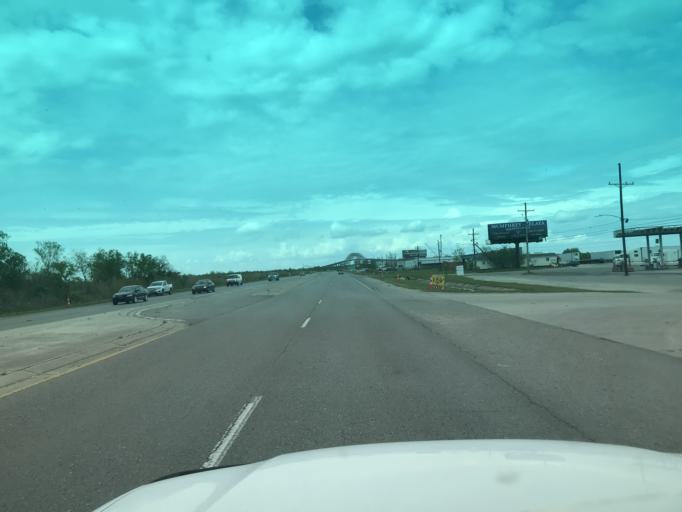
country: US
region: Louisiana
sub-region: Saint Bernard Parish
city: Chalmette
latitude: 29.9830
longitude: -89.9451
